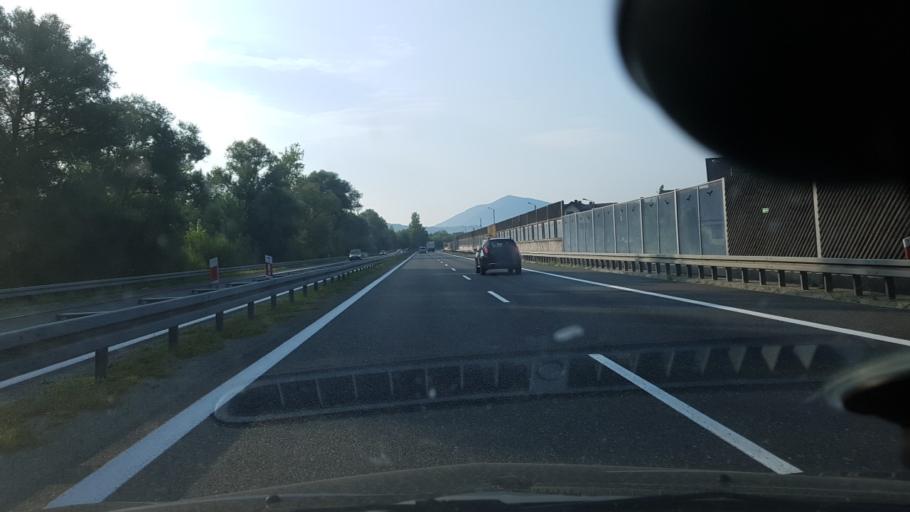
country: PL
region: Lesser Poland Voivodeship
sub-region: Powiat myslenicki
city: Pcim
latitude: 49.7659
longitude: 19.9633
